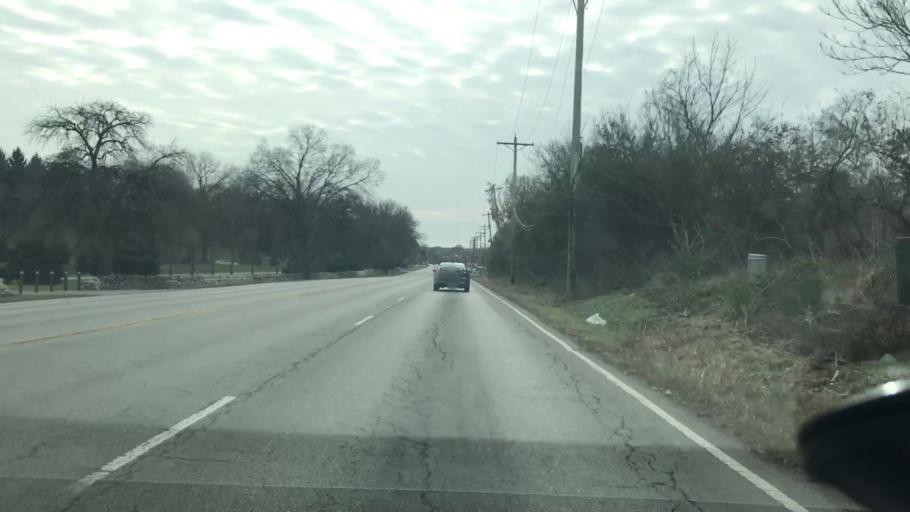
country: US
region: Ohio
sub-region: Franklin County
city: Upper Arlington
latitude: 40.0026
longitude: -83.0790
